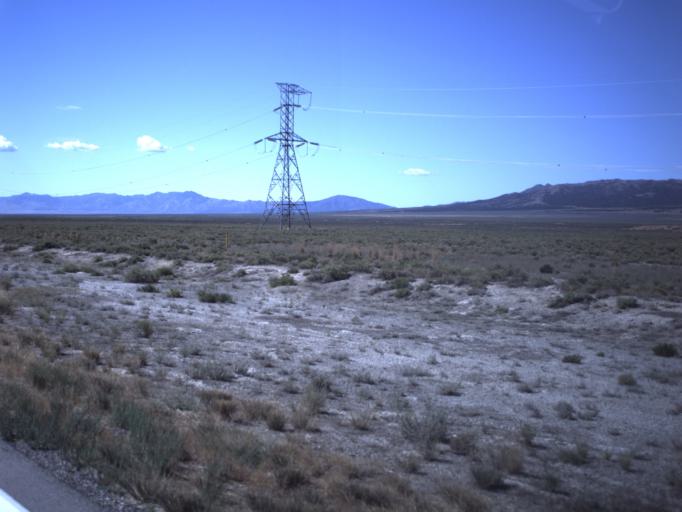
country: US
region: Utah
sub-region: Tooele County
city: Tooele
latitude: 40.2966
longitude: -112.4018
